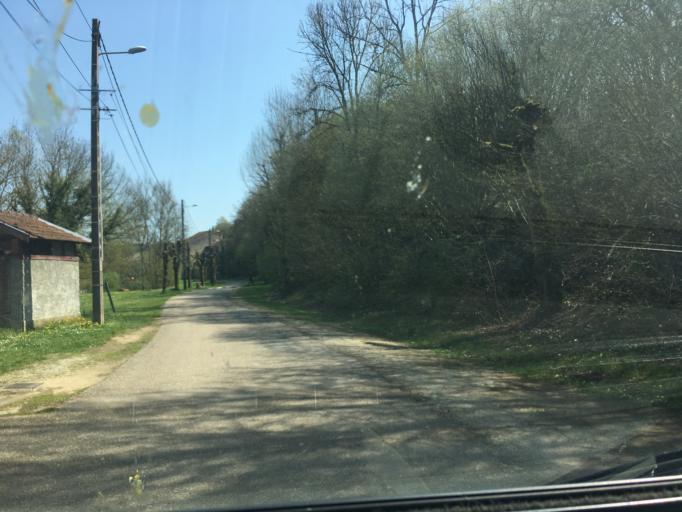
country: FR
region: Lorraine
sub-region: Departement de Meurthe-et-Moselle
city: Pagny-sur-Moselle
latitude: 48.9516
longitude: 5.8632
